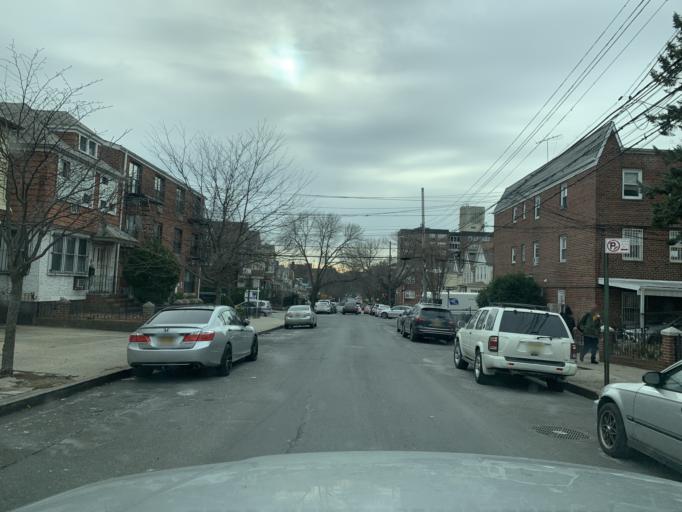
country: US
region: New York
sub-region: Queens County
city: Borough of Queens
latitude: 40.7385
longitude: -73.8708
